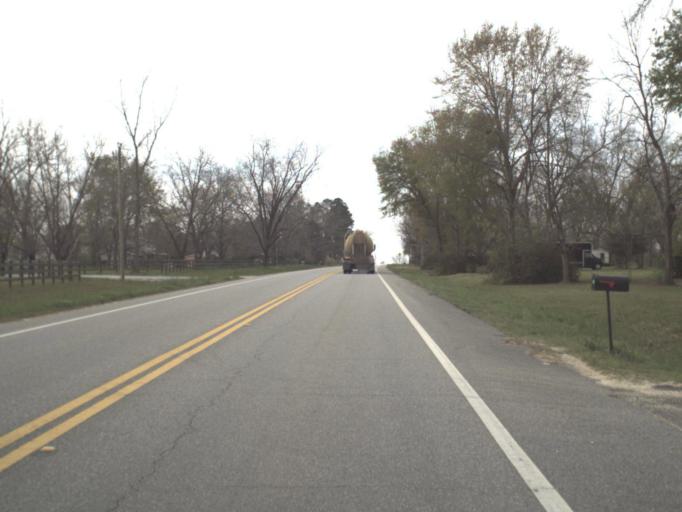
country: US
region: Florida
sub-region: Holmes County
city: Bonifay
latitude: 30.9127
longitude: -85.6499
